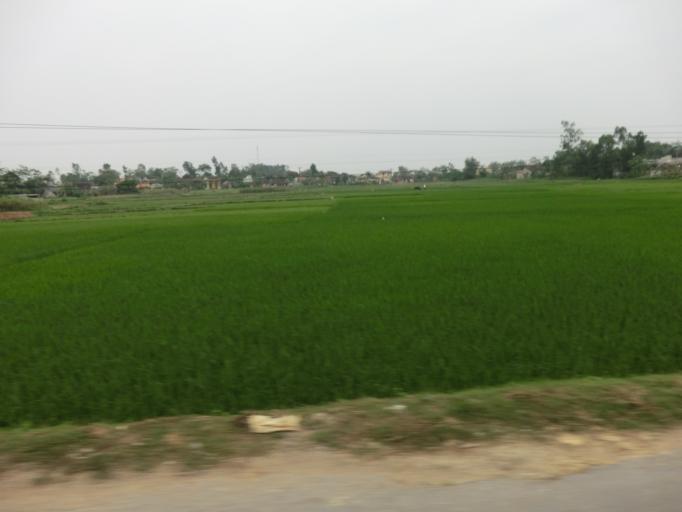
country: VN
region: Nghe An
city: Cau Giat
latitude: 19.2100
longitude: 105.5514
